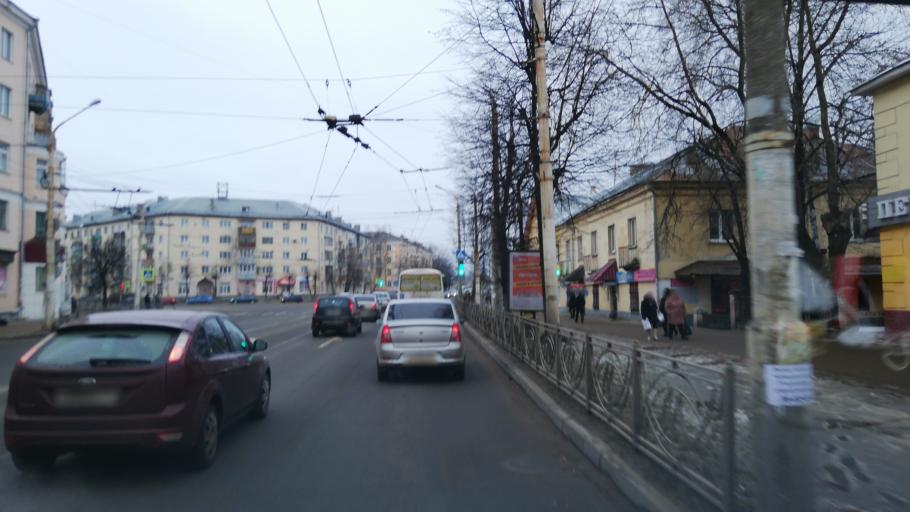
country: RU
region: Kostroma
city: Oktyabr'skiy
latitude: 57.7578
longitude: 40.9721
